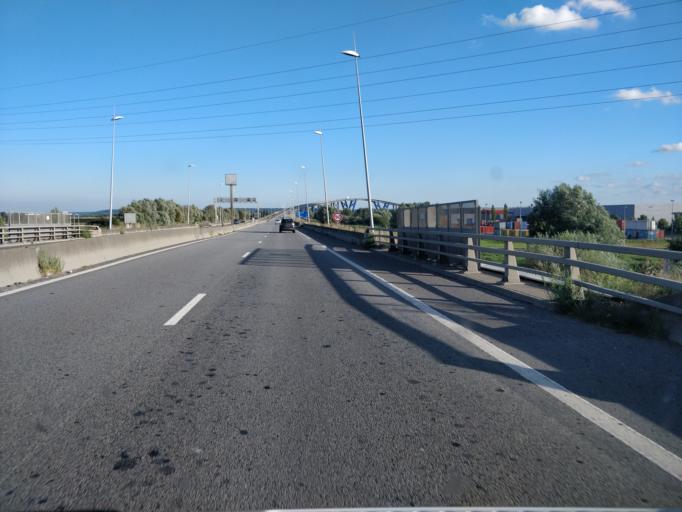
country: FR
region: Haute-Normandie
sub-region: Departement de la Seine-Maritime
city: Rogerville
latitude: 49.4774
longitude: 0.2662
